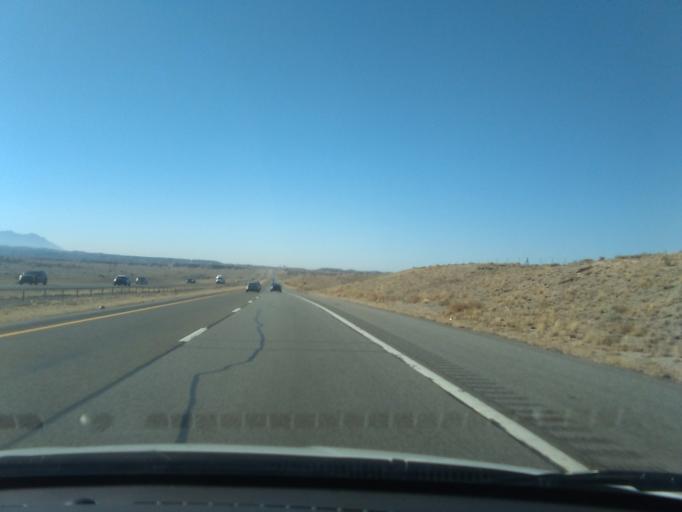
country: US
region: New Mexico
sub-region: Sandoval County
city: Santo Domingo Pueblo
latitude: 35.4453
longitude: -106.3643
